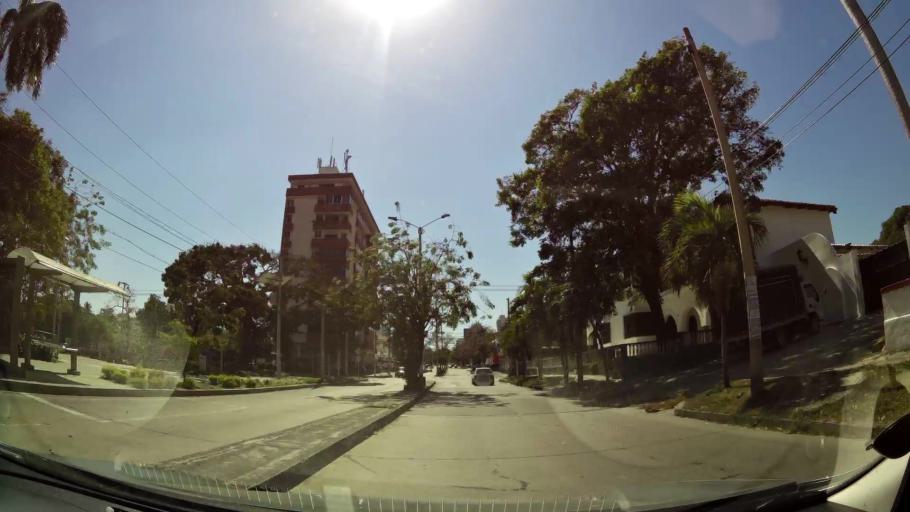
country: CO
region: Atlantico
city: Barranquilla
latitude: 11.0031
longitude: -74.7960
